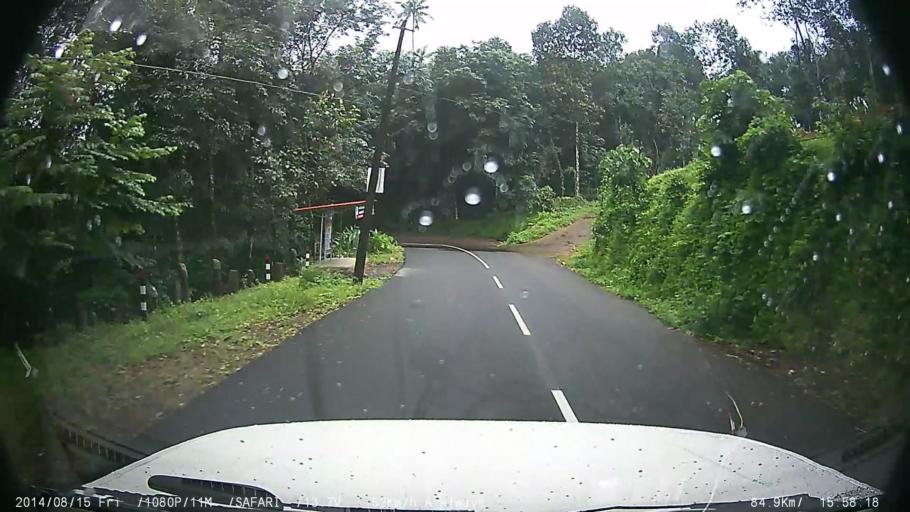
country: IN
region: Kerala
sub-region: Kottayam
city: Lalam
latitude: 9.7803
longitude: 76.7254
